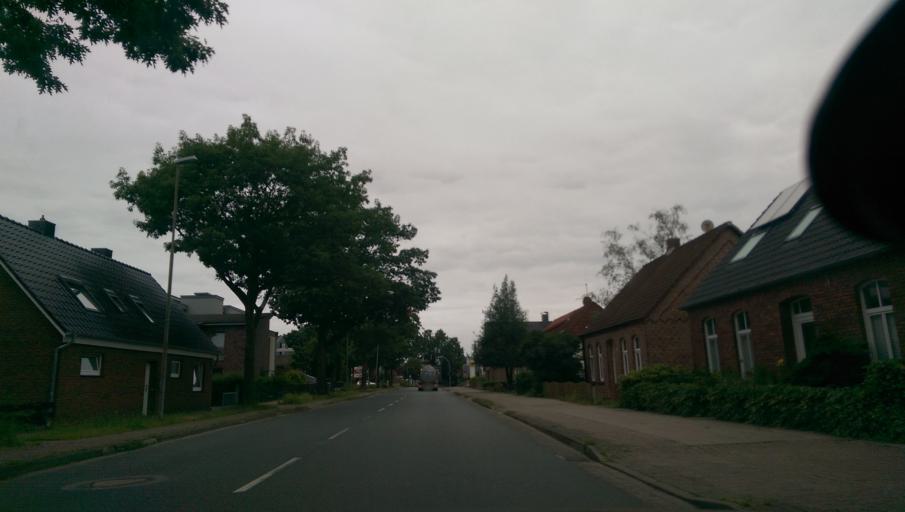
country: DE
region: Lower Saxony
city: Rotenburg
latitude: 53.1011
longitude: 9.3997
